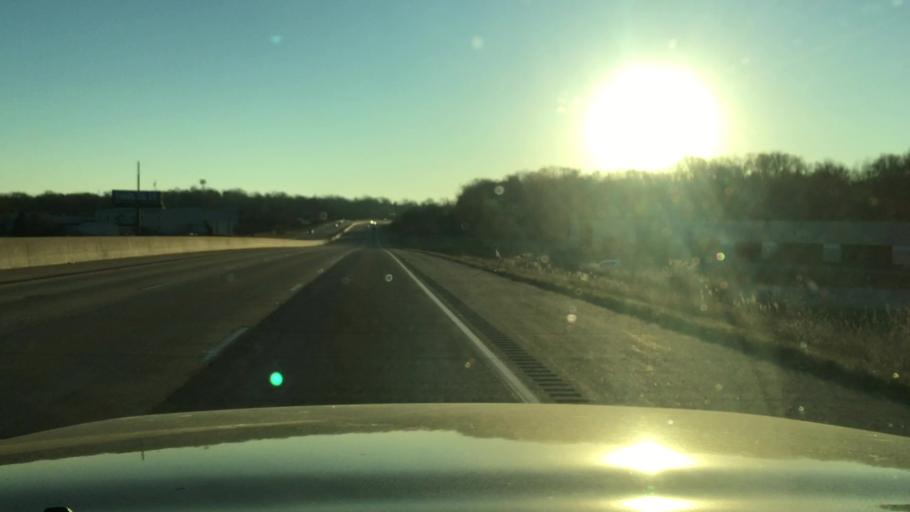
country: US
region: Missouri
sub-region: Saint Charles County
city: Saint Charles
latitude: 38.8207
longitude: -90.5058
